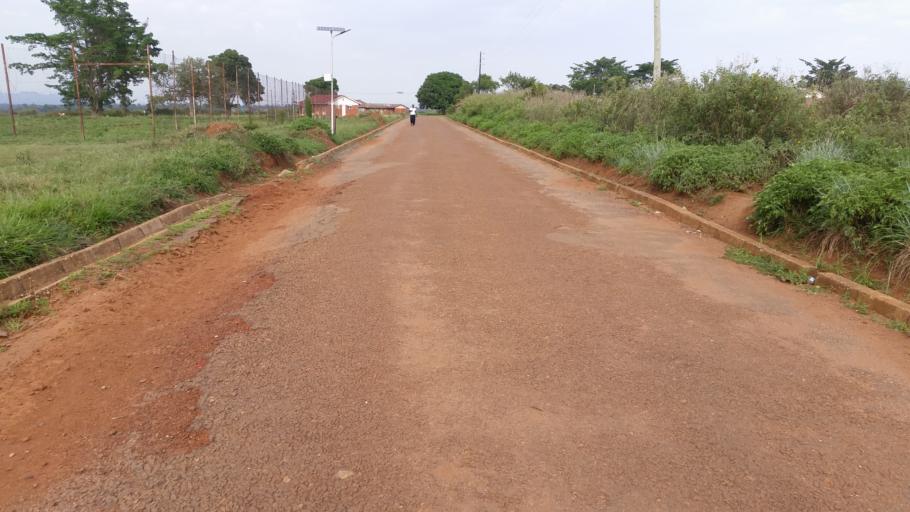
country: UG
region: Eastern Region
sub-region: Busia District
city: Busia
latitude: 0.5461
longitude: 34.0231
